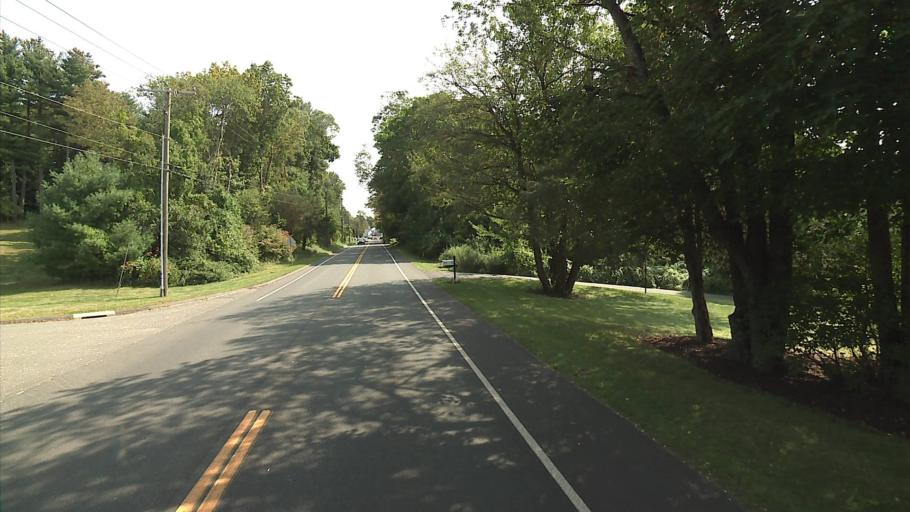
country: US
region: Connecticut
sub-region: Fairfield County
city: Bethel
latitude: 41.3819
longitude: -73.3597
